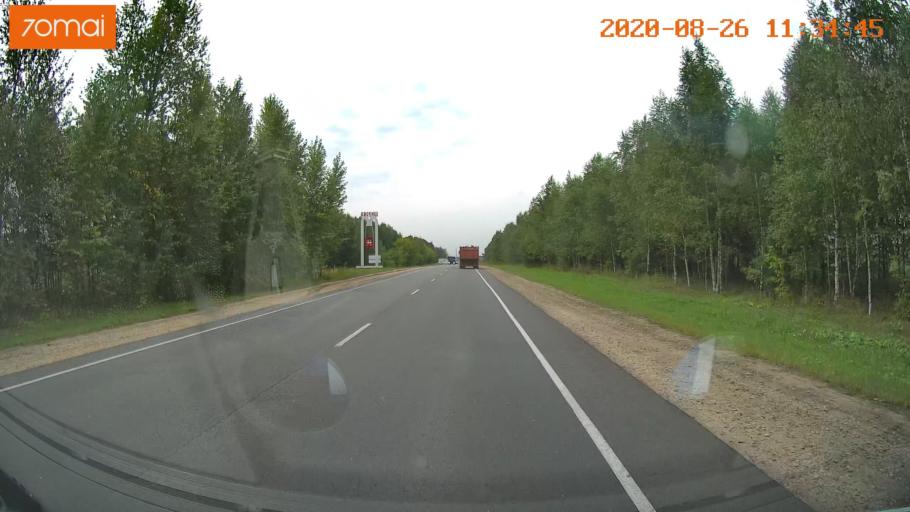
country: RU
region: Rjazan
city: Shilovo
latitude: 54.2816
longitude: 40.8402
